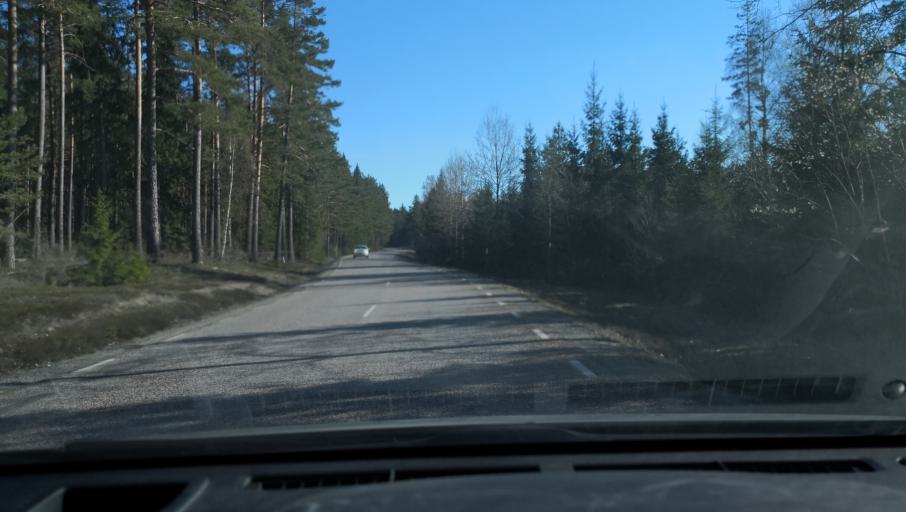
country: SE
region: Dalarna
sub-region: Avesta Kommun
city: Avesta
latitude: 60.0255
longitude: 16.3347
